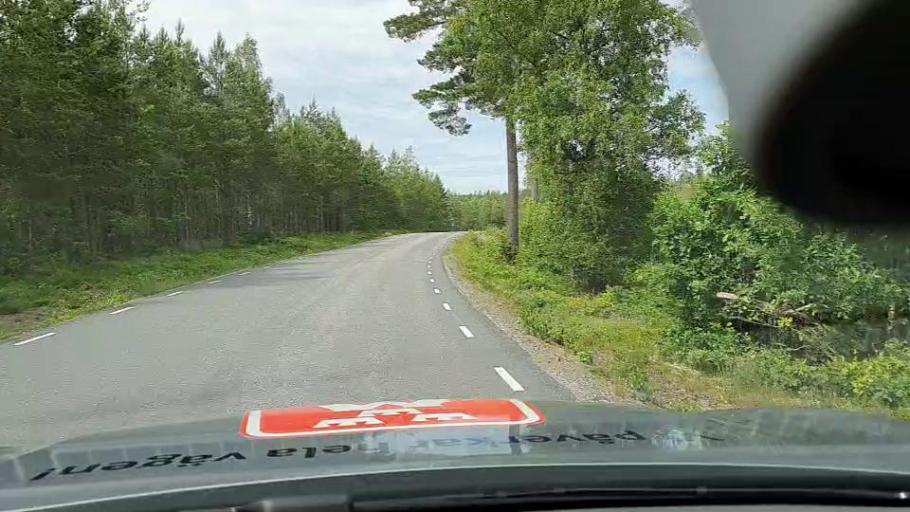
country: SE
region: Soedermanland
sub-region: Eskilstuna Kommun
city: Arla
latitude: 59.2427
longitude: 16.7193
